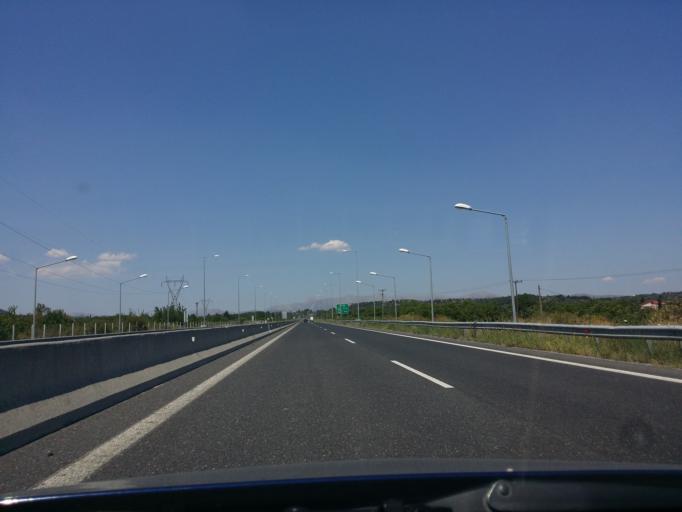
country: GR
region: Peloponnese
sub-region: Nomos Arkadias
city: Tripoli
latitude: 37.4680
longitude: 22.3330
